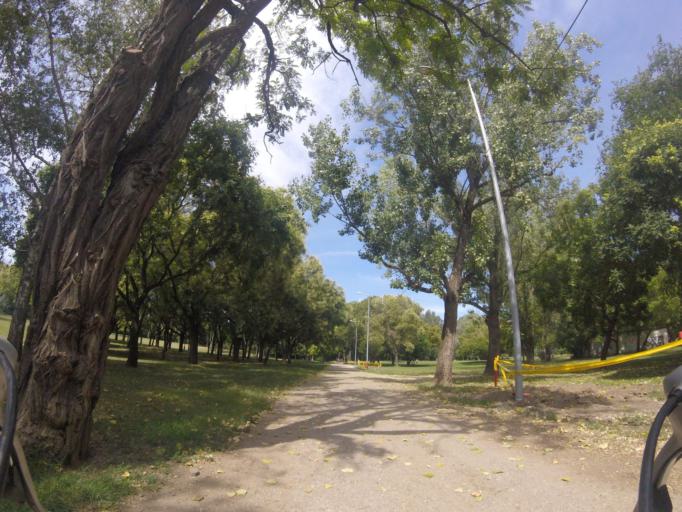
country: HU
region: Budapest
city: Budapest III. keruelet
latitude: 47.5573
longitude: 19.0589
